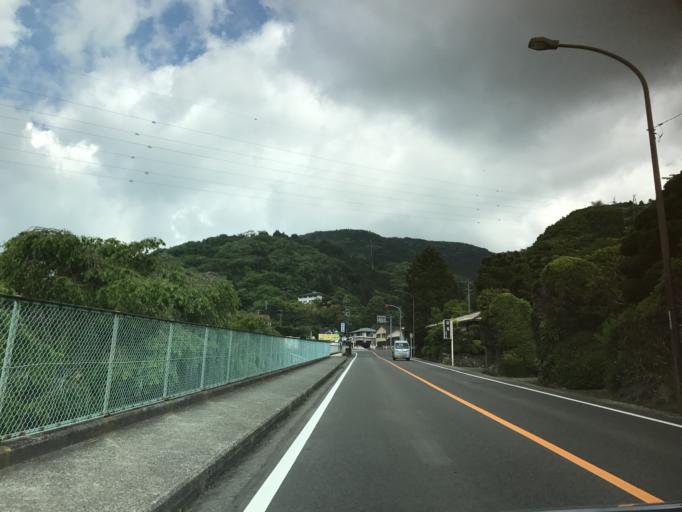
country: JP
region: Kanagawa
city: Hakone
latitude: 35.2557
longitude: 139.0482
